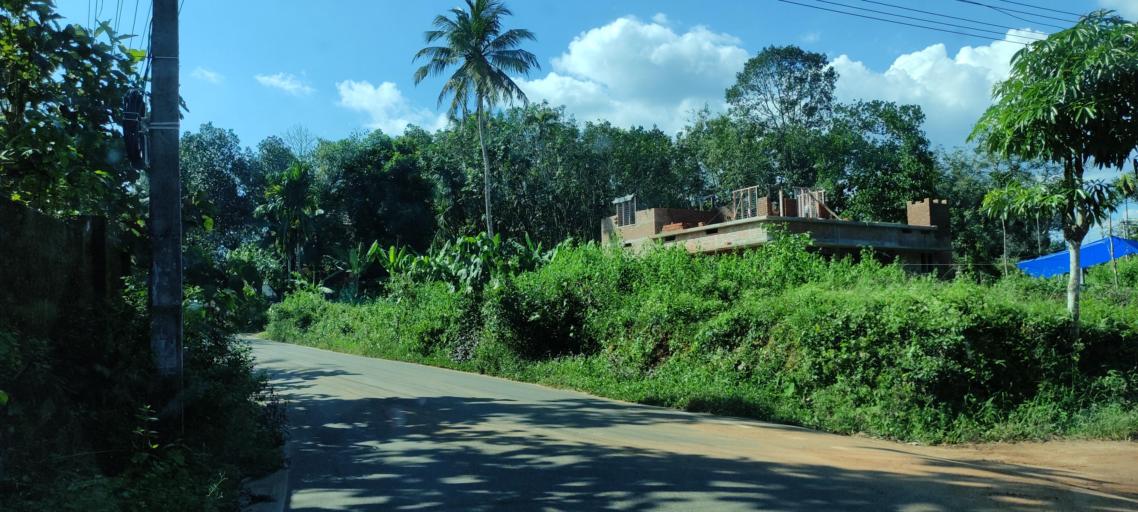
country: IN
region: Kerala
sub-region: Pattanamtitta
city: Adur
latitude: 9.2005
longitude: 76.7520
